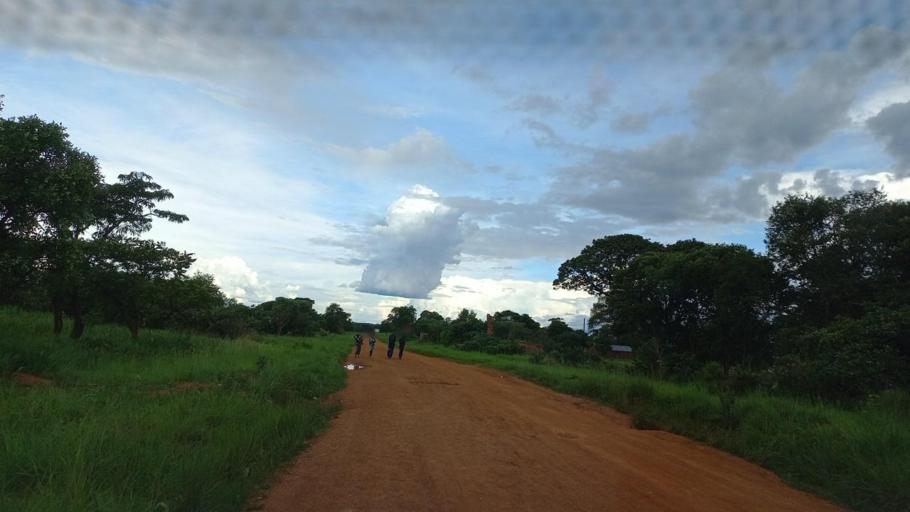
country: ZM
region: North-Western
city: Mwinilunga
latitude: -11.7585
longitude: 24.4234
